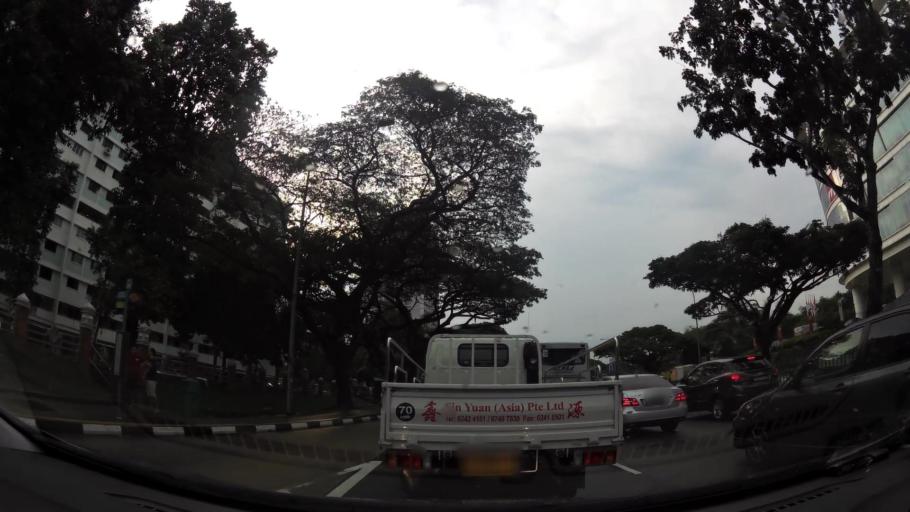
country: SG
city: Singapore
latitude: 1.3757
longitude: 103.8558
